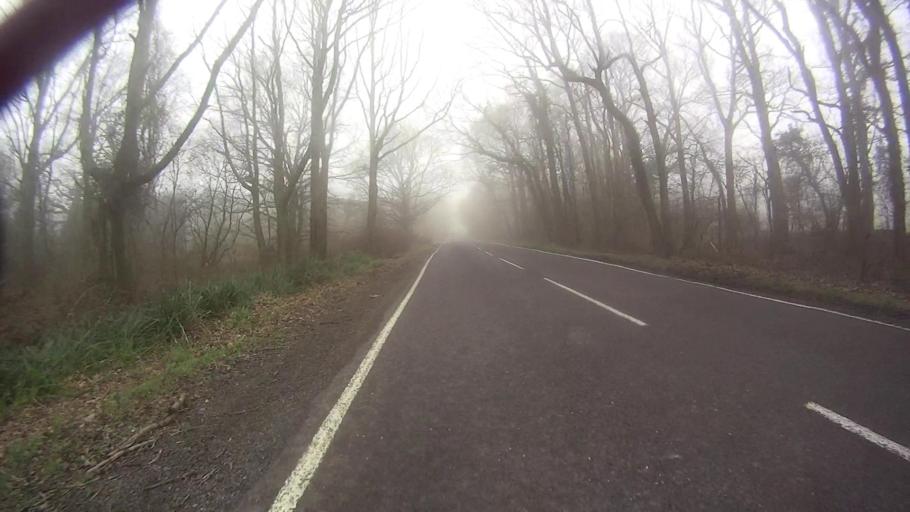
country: GB
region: England
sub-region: Surrey
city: Newdigate
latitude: 51.1428
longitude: -0.3225
